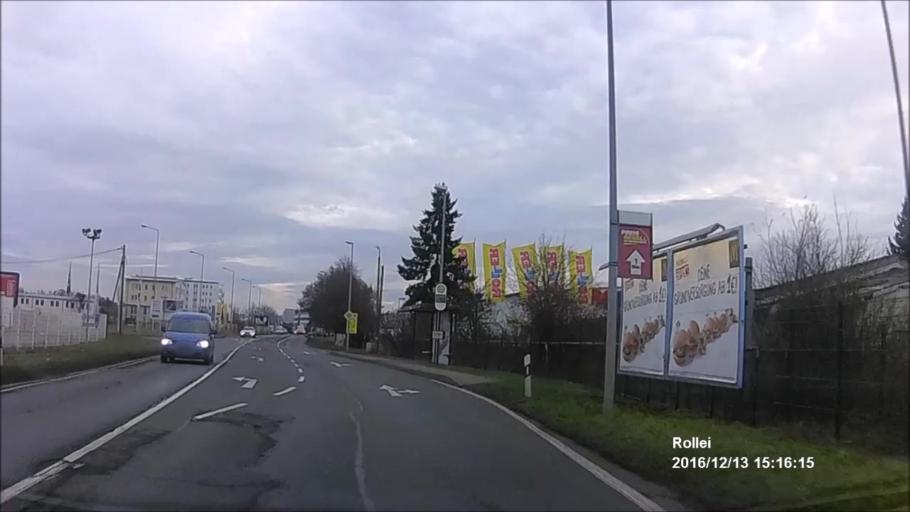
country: DE
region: Thuringia
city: Noda
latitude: 51.0218
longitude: 11.0100
